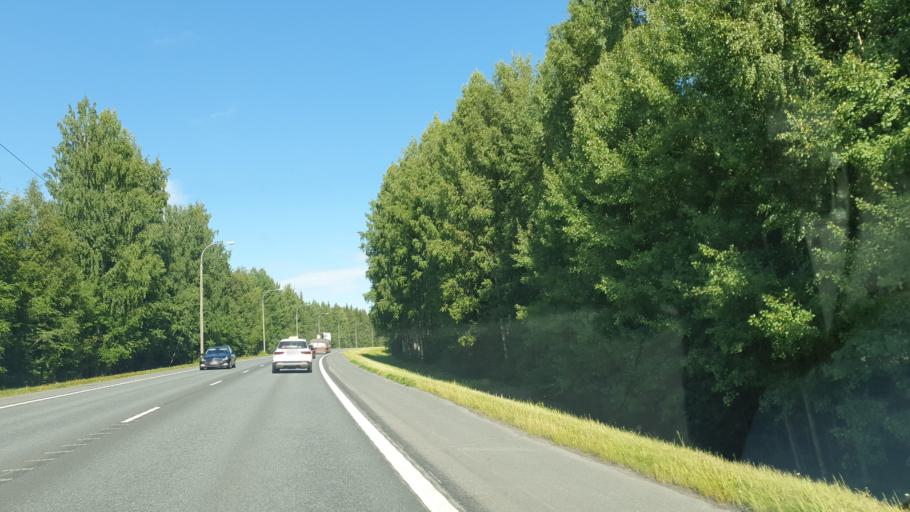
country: FI
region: Northern Savo
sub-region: Ylae-Savo
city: Iisalmi
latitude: 63.5060
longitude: 27.2587
